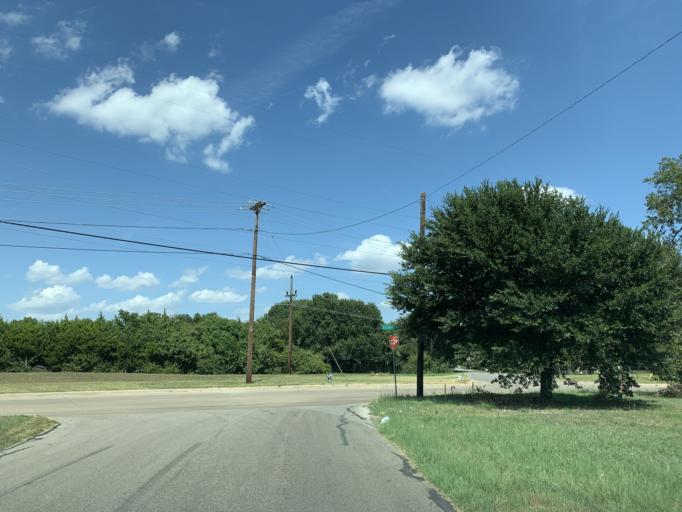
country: US
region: Texas
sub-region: Dallas County
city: Hutchins
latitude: 32.7060
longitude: -96.7675
